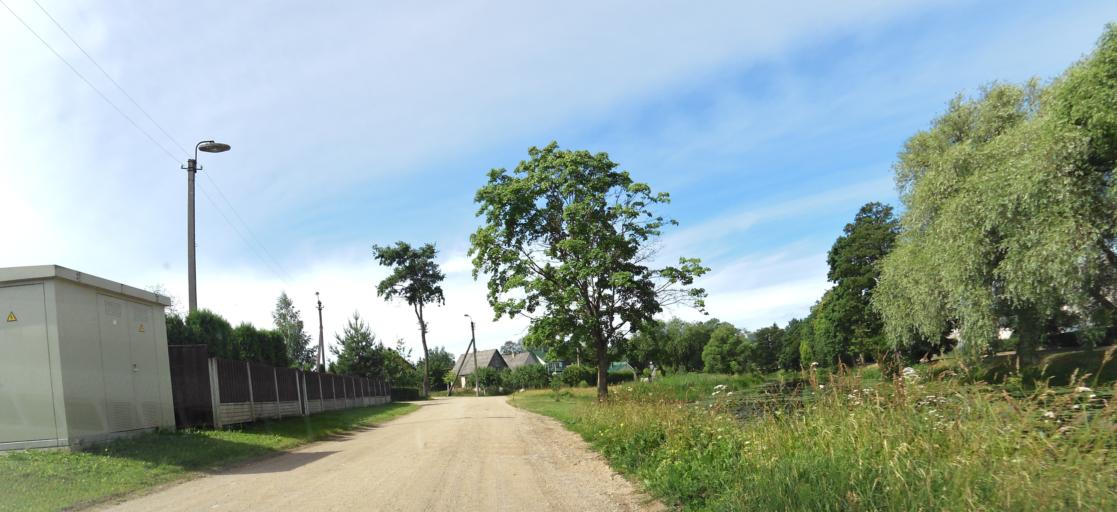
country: LT
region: Panevezys
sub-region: Birzai
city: Birzai
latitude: 56.1992
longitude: 24.7643
